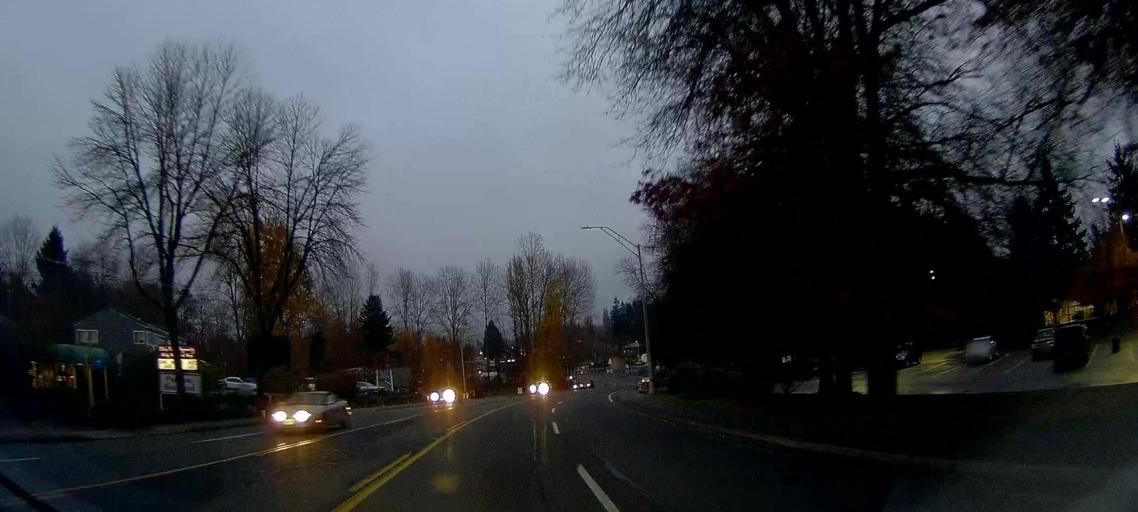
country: US
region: Washington
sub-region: Thurston County
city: Olympia
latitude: 47.0445
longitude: -122.8645
